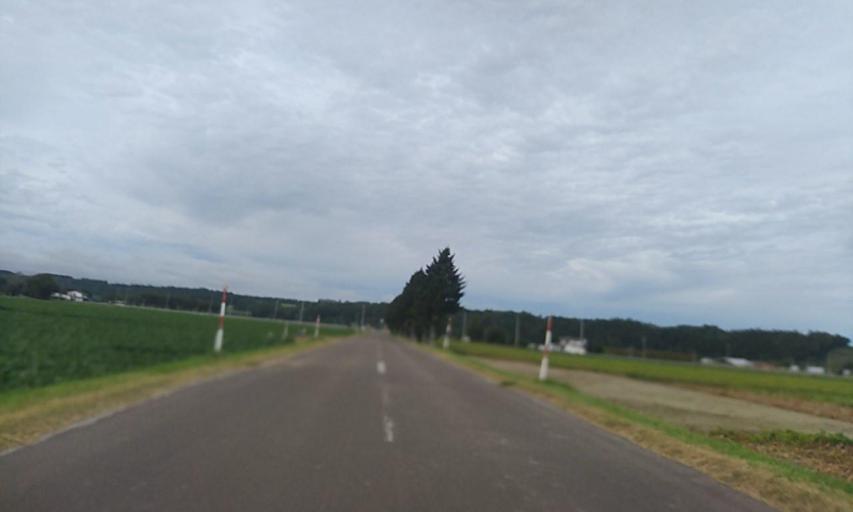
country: JP
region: Hokkaido
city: Abashiri
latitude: 43.7949
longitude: 144.5420
